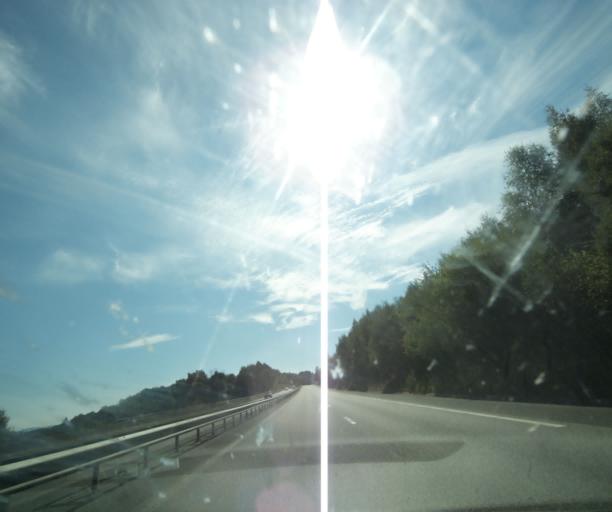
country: FR
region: Limousin
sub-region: Departement de la Correze
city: Donzenac
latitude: 45.2583
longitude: 1.5437
